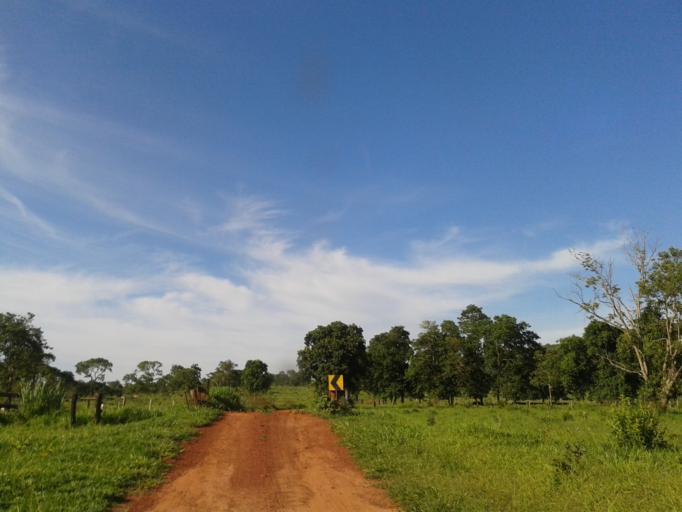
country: BR
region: Minas Gerais
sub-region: Santa Vitoria
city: Santa Vitoria
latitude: -19.0833
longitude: -49.9606
